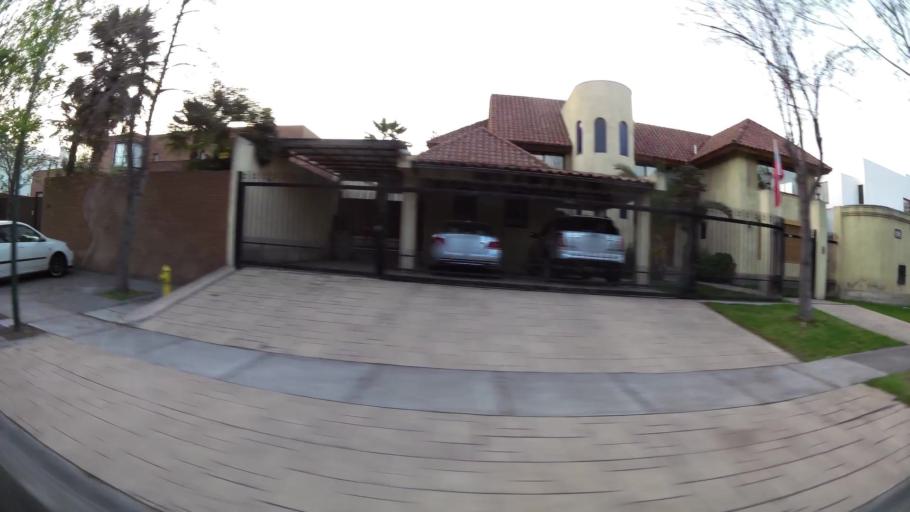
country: CL
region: Santiago Metropolitan
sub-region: Provincia de Chacabuco
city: Chicureo Abajo
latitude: -33.3354
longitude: -70.5450
